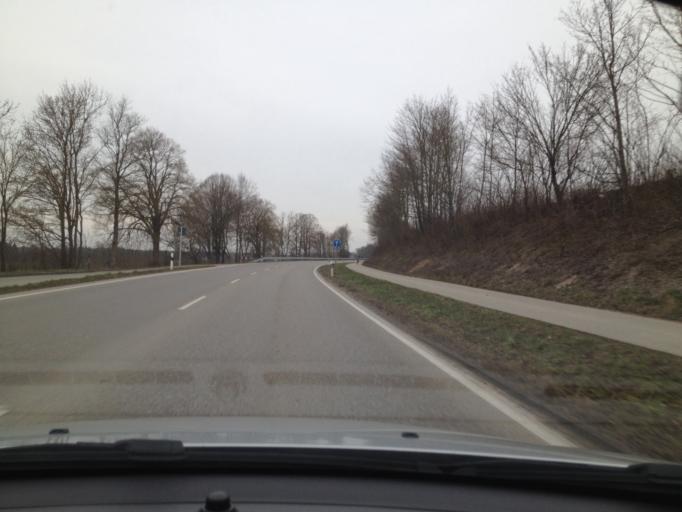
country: DE
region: Bavaria
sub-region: Swabia
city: Bobingen
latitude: 48.2983
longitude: 10.8510
